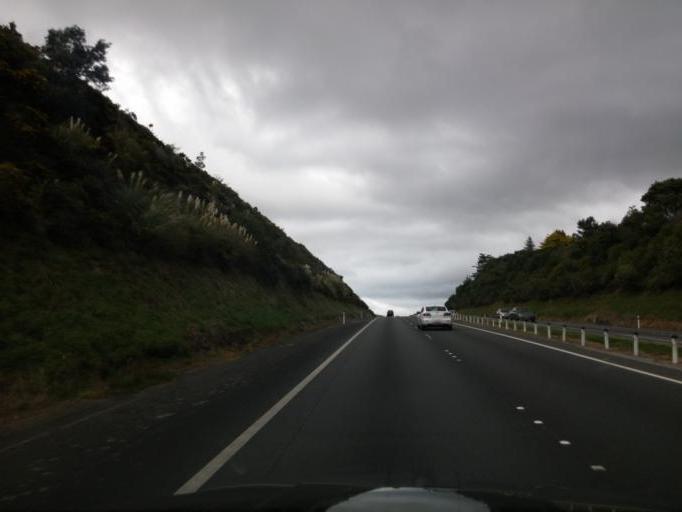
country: NZ
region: Wellington
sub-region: Porirua City
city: Porirua
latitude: -41.1703
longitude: 174.8316
